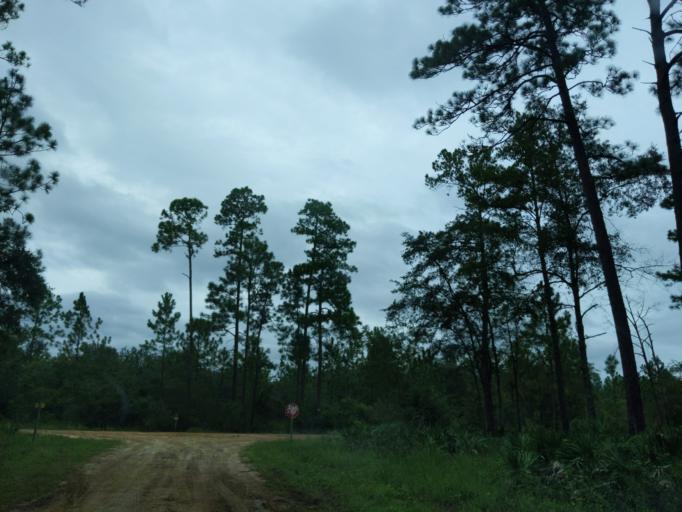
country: US
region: Florida
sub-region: Gadsden County
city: Midway
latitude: 30.3998
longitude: -84.4646
